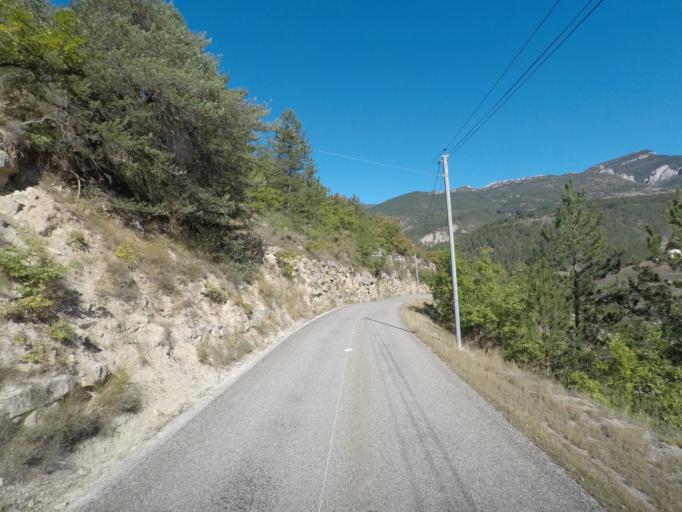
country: FR
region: Rhone-Alpes
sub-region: Departement de la Drome
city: Die
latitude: 44.6213
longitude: 5.3055
